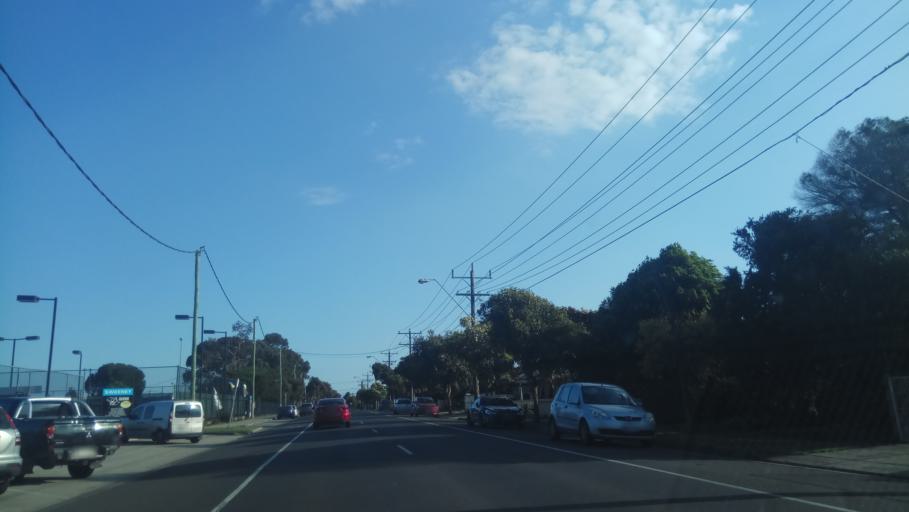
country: AU
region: Victoria
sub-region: Hobsons Bay
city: Laverton
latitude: -37.8631
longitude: 144.7788
